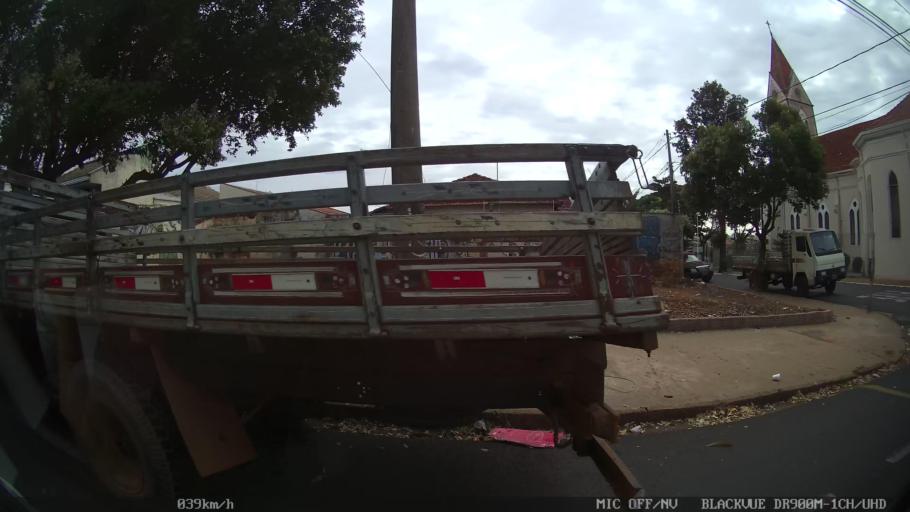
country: BR
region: Sao Paulo
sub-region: Sao Jose Do Rio Preto
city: Sao Jose do Rio Preto
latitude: -20.8152
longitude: -49.3709
